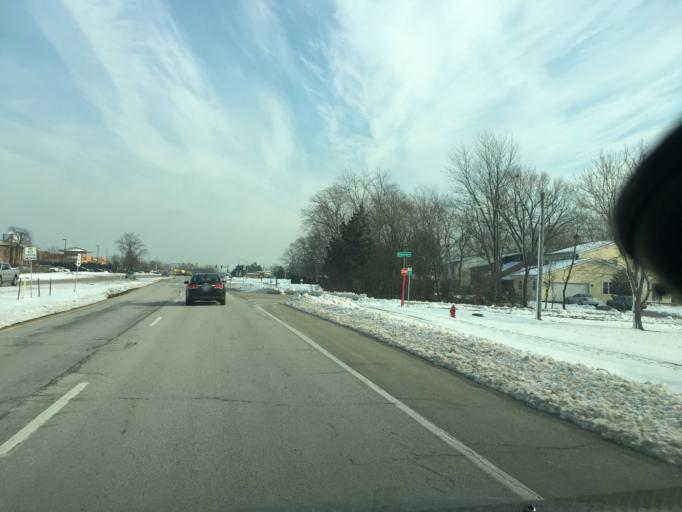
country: US
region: Illinois
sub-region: DuPage County
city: Willowbrook
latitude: 41.7522
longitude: -87.9489
